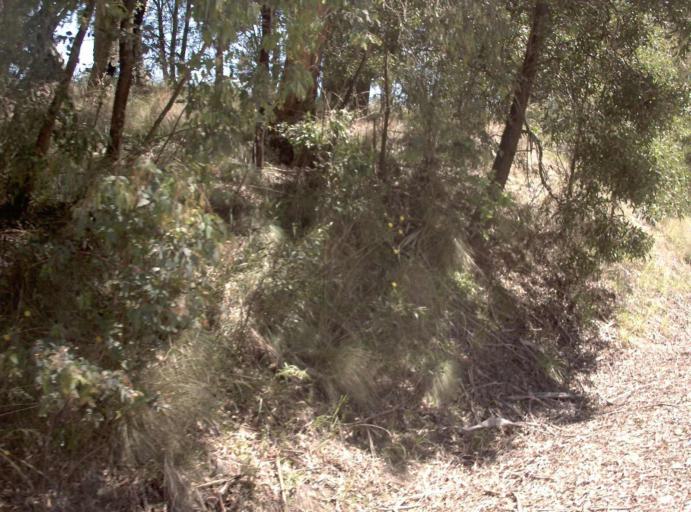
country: AU
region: Victoria
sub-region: East Gippsland
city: Lakes Entrance
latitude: -37.2162
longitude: 148.2674
